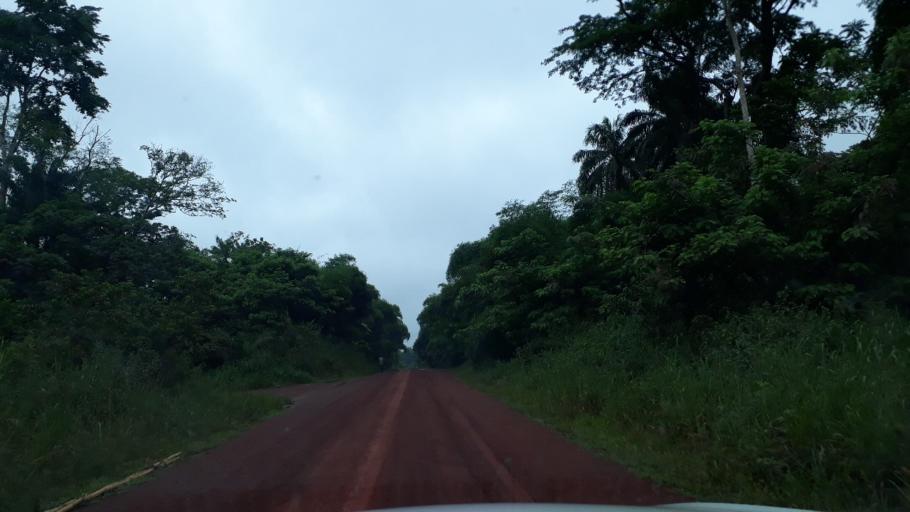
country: CD
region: Eastern Province
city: Wamba
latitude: 1.3807
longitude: 27.5986
